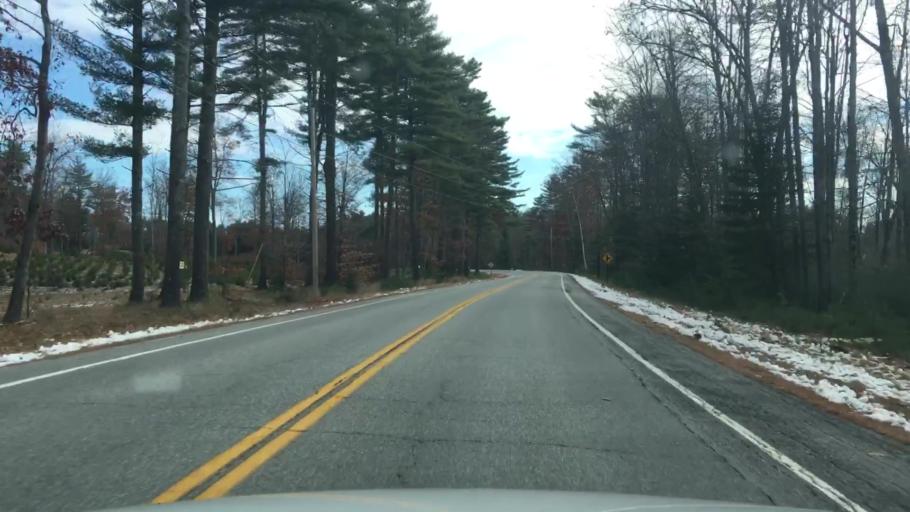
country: US
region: Maine
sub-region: Kennebec County
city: Wayne
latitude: 44.3511
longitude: -70.1048
